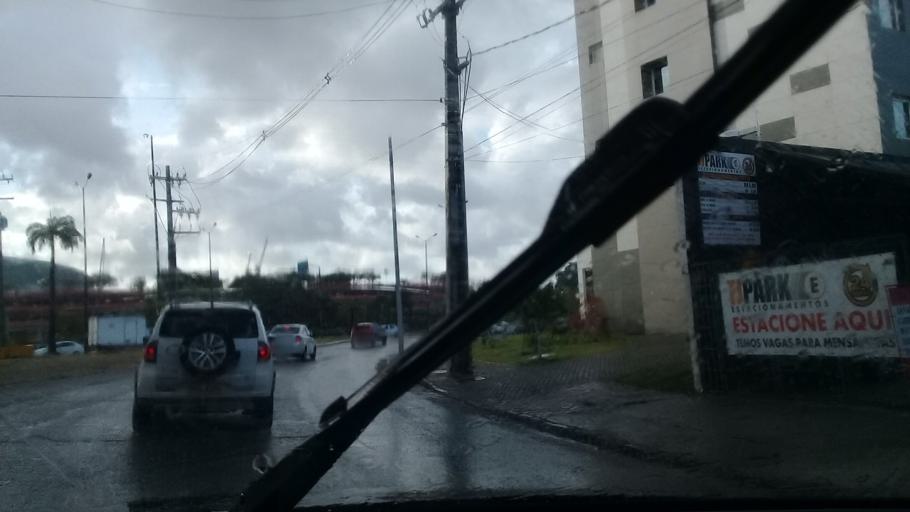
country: BR
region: Pernambuco
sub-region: Recife
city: Recife
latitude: -8.1324
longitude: -34.9156
